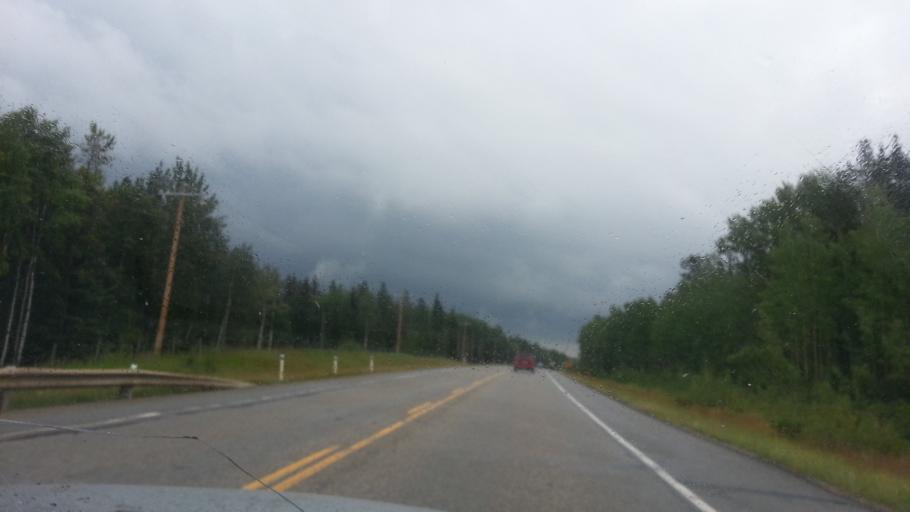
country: CA
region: Alberta
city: Cochrane
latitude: 50.9217
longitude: -114.5741
